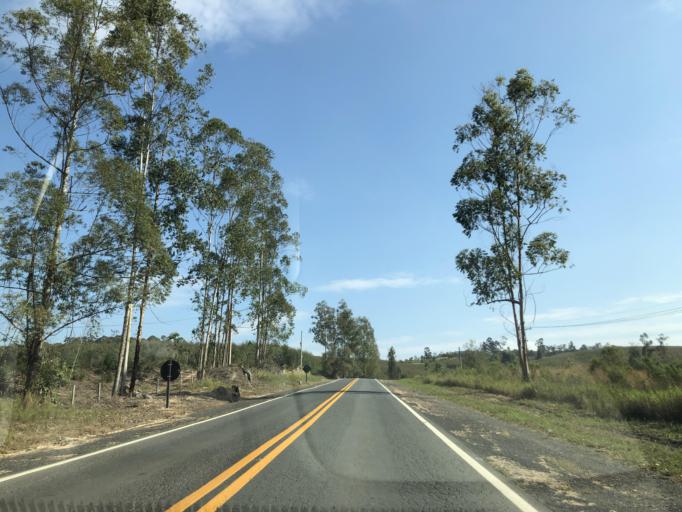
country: BR
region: Sao Paulo
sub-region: Pilar Do Sul
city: Pilar do Sul
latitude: -23.8290
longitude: -47.6659
